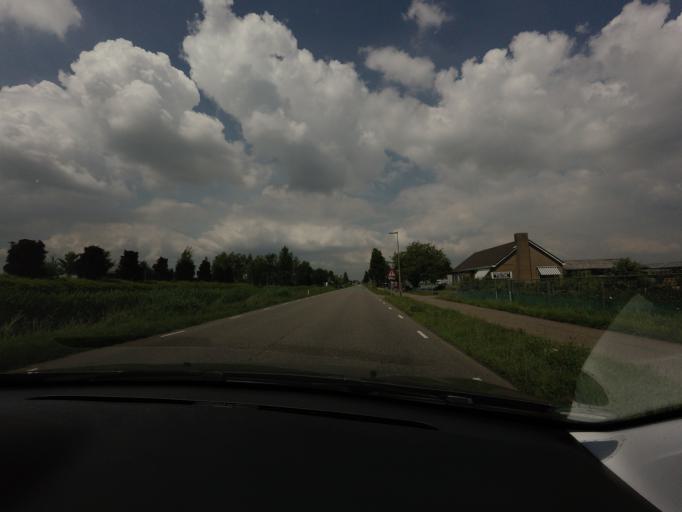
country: NL
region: South Holland
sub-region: Gemeente Barendrecht
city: Barendrecht
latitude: 51.8369
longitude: 4.5363
